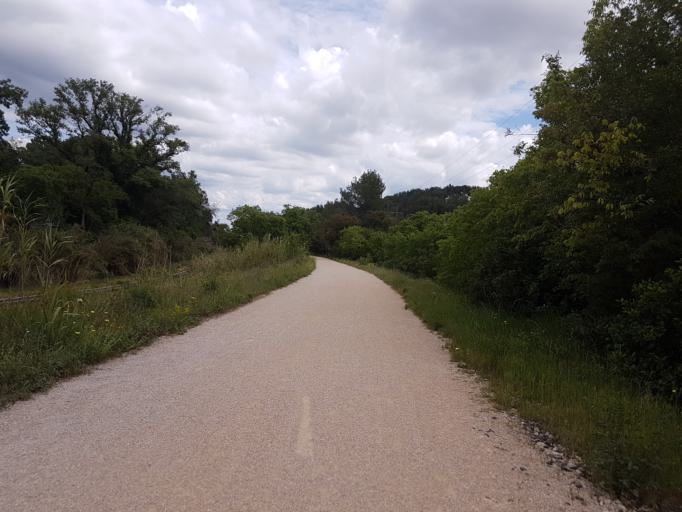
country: FR
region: Languedoc-Roussillon
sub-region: Departement du Gard
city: Vallabregues
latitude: 43.8276
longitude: 4.6217
